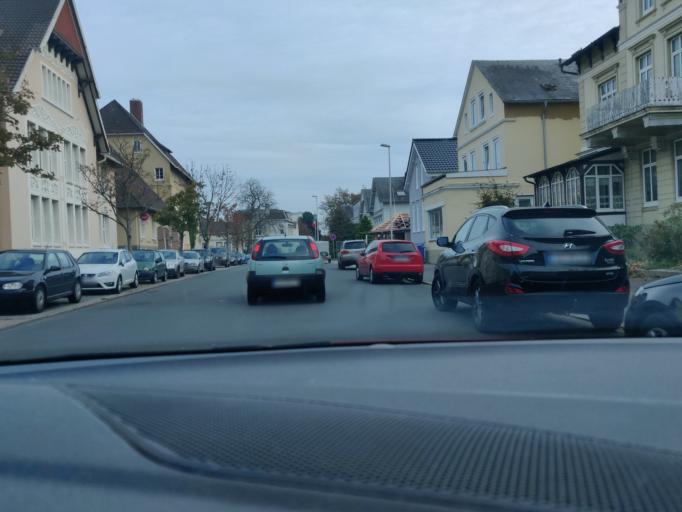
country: DE
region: Lower Saxony
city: Cuxhaven
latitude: 53.8726
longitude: 8.6965
